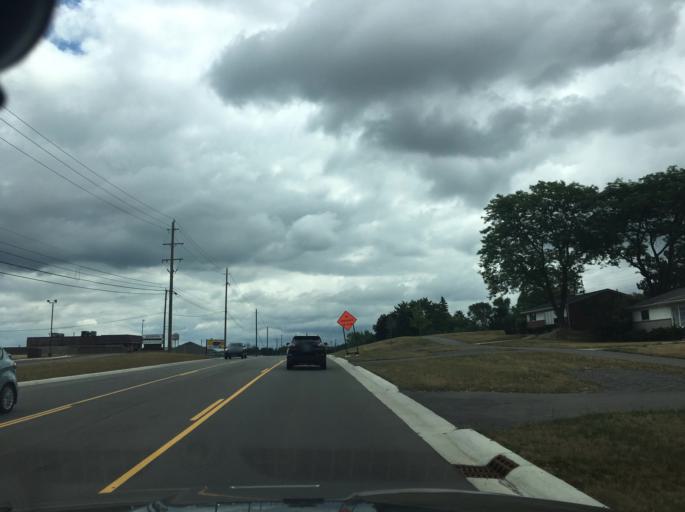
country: US
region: Michigan
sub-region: Oakland County
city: Rochester
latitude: 42.6955
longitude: -83.1412
